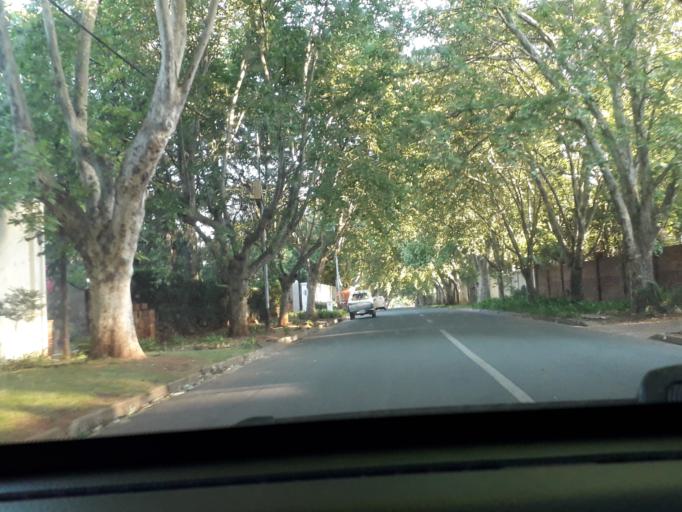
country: ZA
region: Gauteng
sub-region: City of Johannesburg Metropolitan Municipality
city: Johannesburg
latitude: -26.1589
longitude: 28.0535
